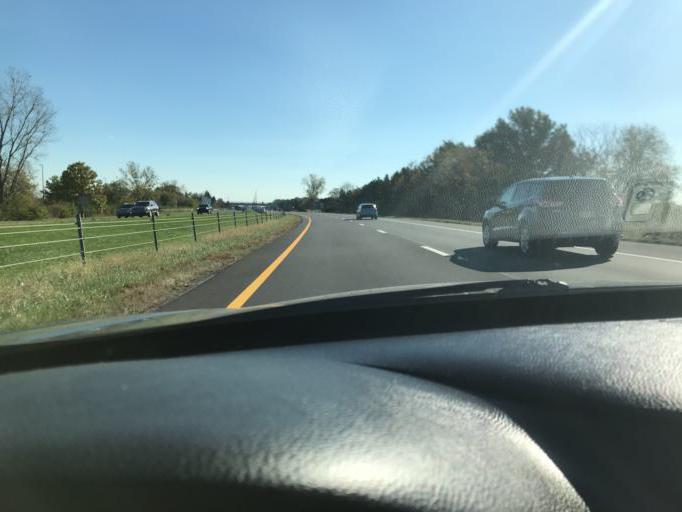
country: US
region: Ohio
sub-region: Franklin County
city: Dublin
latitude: 40.0992
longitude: -83.1672
